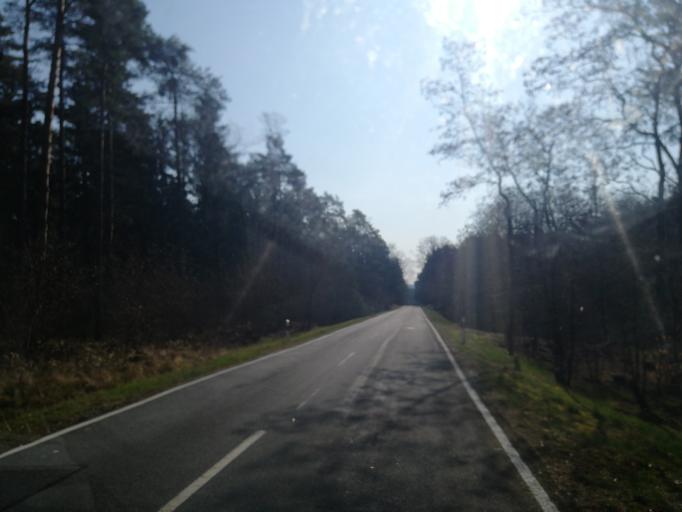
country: DE
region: Brandenburg
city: Sonnewalde
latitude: 51.7596
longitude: 13.6652
